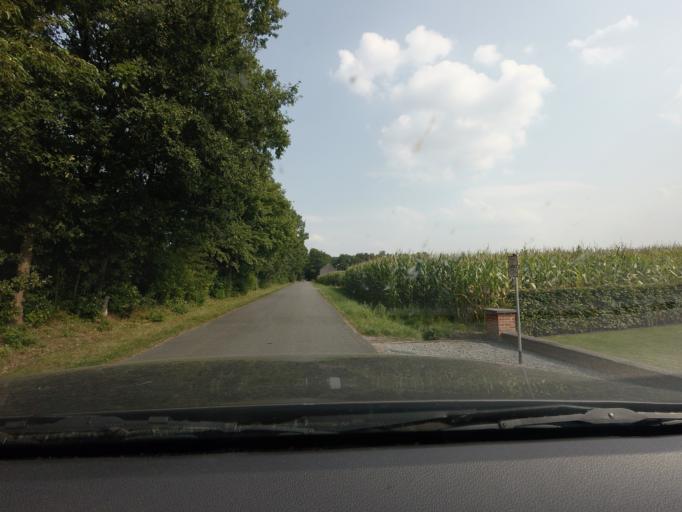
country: BE
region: Flanders
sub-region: Provincie Limburg
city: Leopoldsburg
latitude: 51.1187
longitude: 5.2361
